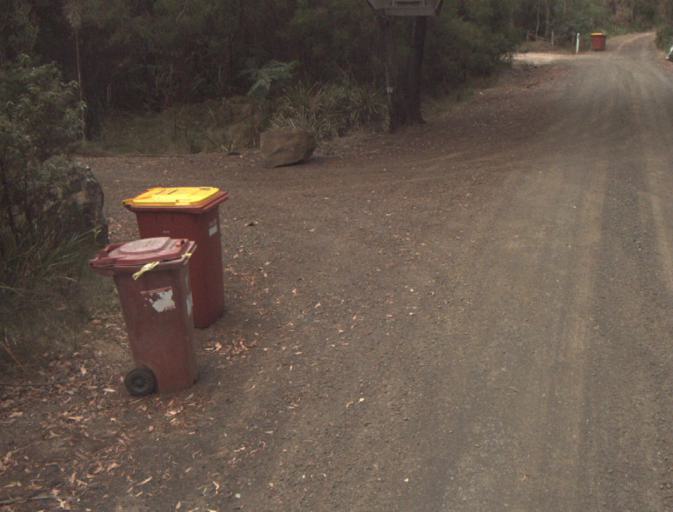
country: AU
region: Tasmania
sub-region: Launceston
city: Mayfield
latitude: -41.2736
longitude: 147.0521
